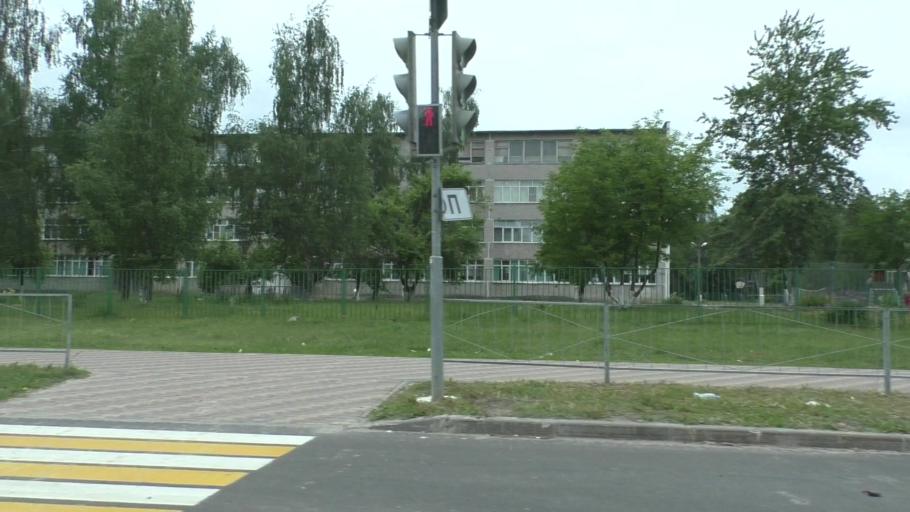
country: RU
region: Moskovskaya
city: Yegor'yevsk
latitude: 55.3667
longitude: 39.0643
